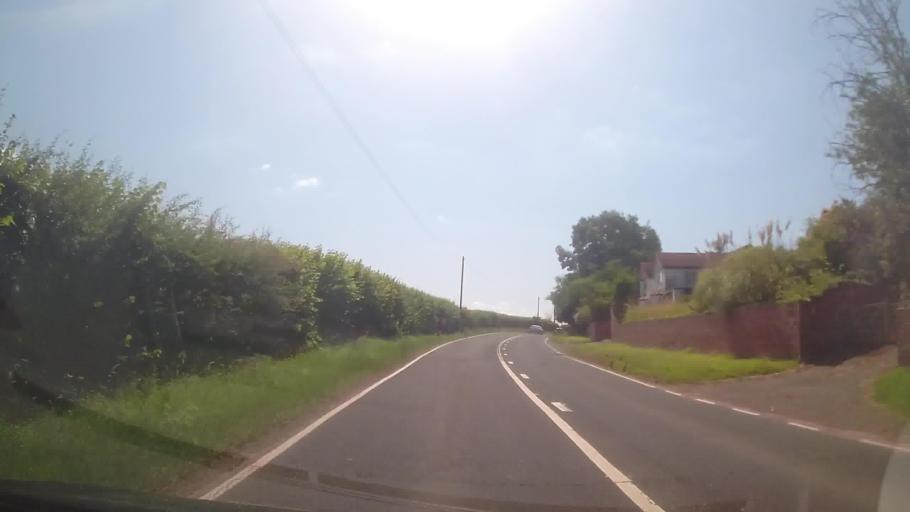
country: GB
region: England
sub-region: Herefordshire
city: Ocle Pychard
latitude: 52.0806
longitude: -2.5984
